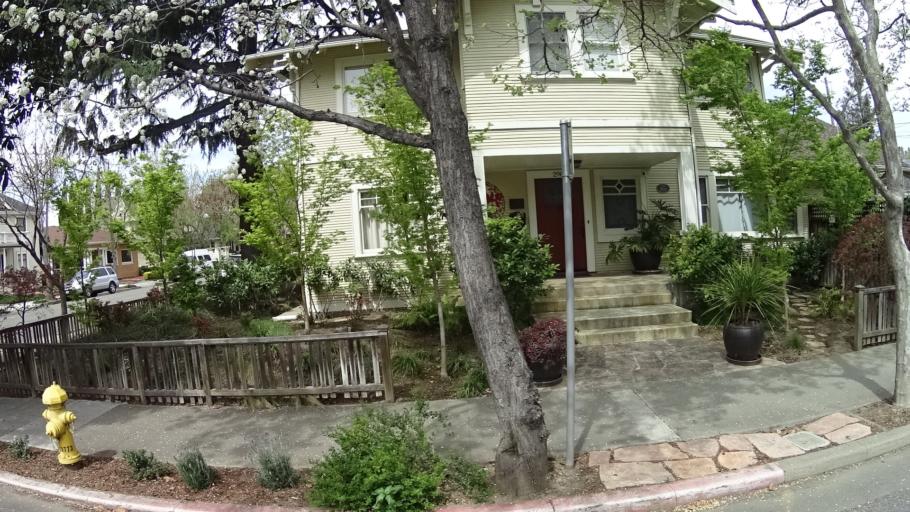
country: US
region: California
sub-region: Santa Clara County
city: San Jose
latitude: 37.3384
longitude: -121.8725
